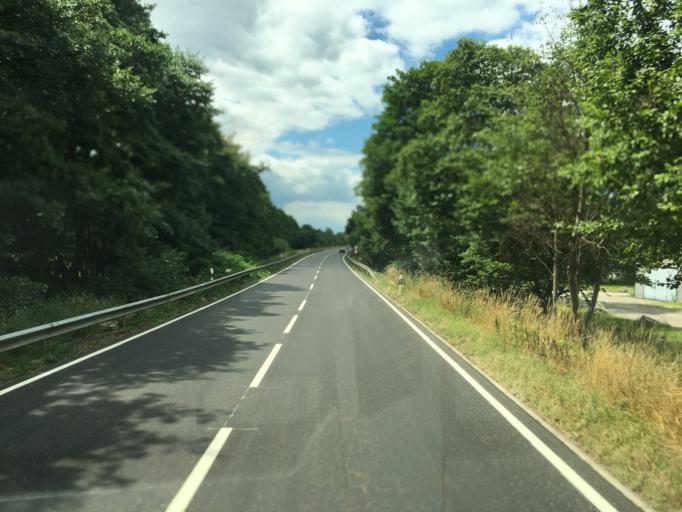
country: DE
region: Baden-Wuerttemberg
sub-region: Karlsruhe Region
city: Ottenhofen
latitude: 48.7283
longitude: 8.1481
